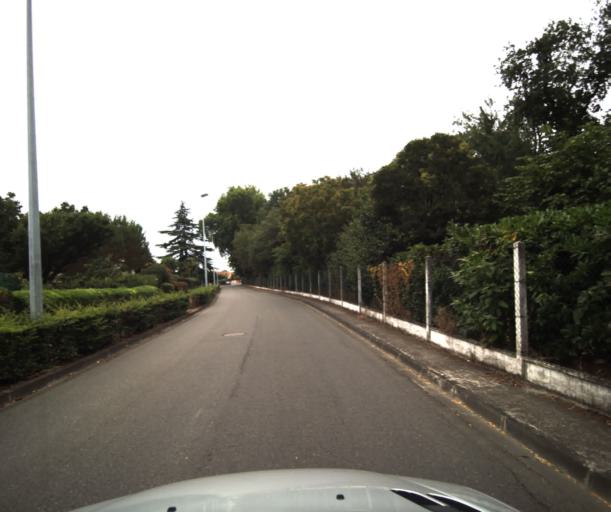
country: FR
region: Midi-Pyrenees
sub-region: Departement de la Haute-Garonne
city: Portet-sur-Garonne
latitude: 43.5267
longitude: 1.4134
